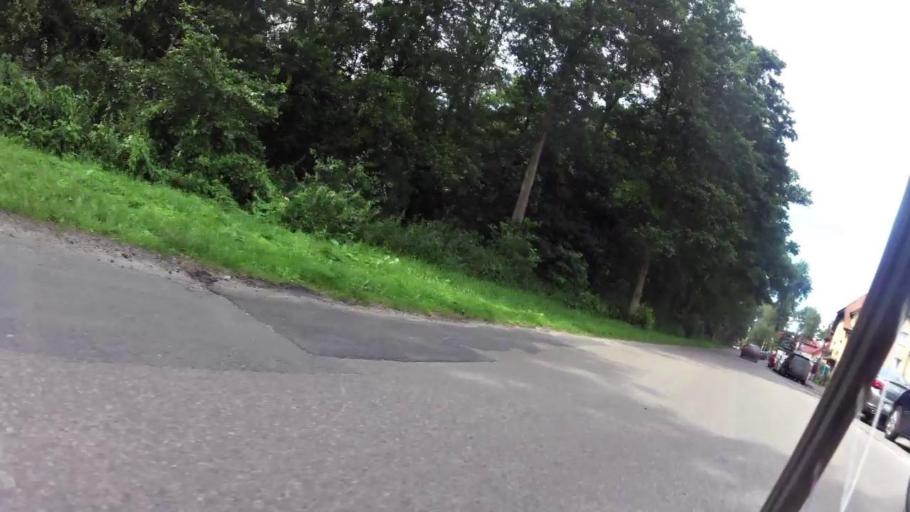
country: PL
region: West Pomeranian Voivodeship
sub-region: Powiat gryficki
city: Pobierowo
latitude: 54.0530
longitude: 14.9292
